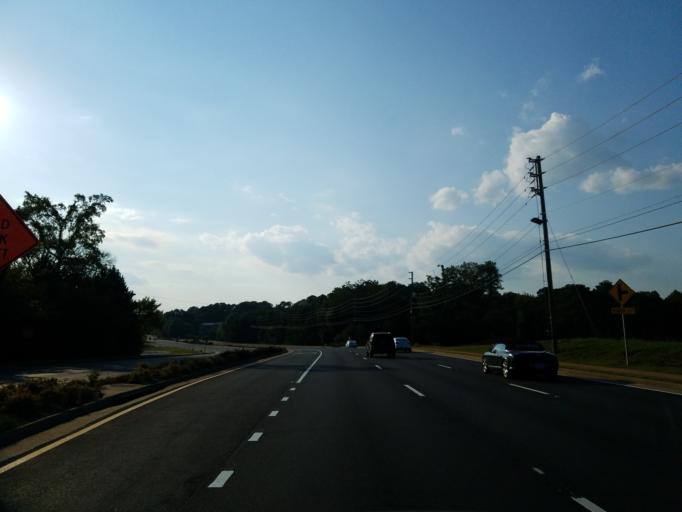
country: US
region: Georgia
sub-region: Fulton County
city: Alpharetta
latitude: 34.0698
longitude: -84.2853
